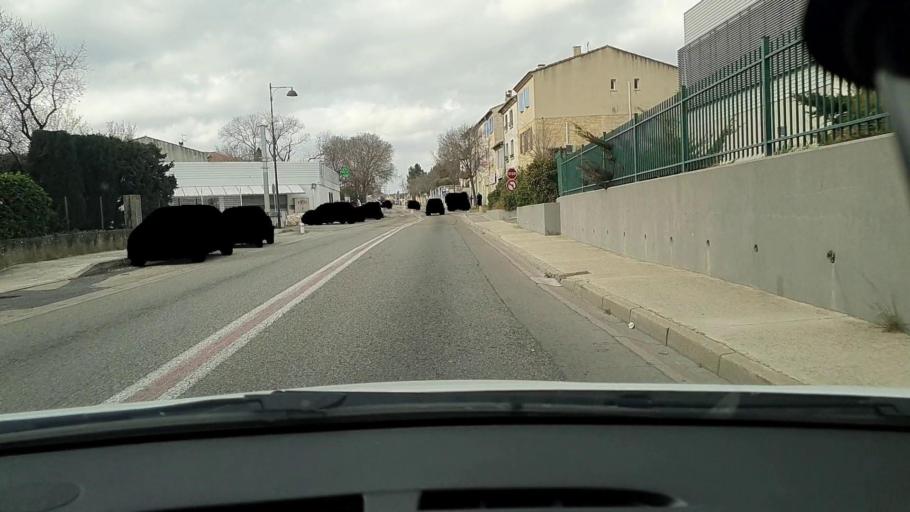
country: FR
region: Languedoc-Roussillon
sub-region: Departement du Gard
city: Beaucaire
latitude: 43.8103
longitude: 4.6371
